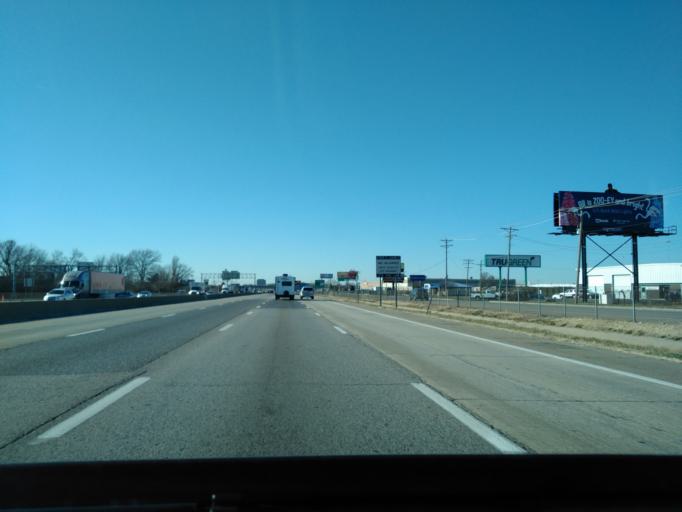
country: US
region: Missouri
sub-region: Saint Louis County
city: Fenton
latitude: 38.5429
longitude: -90.4456
